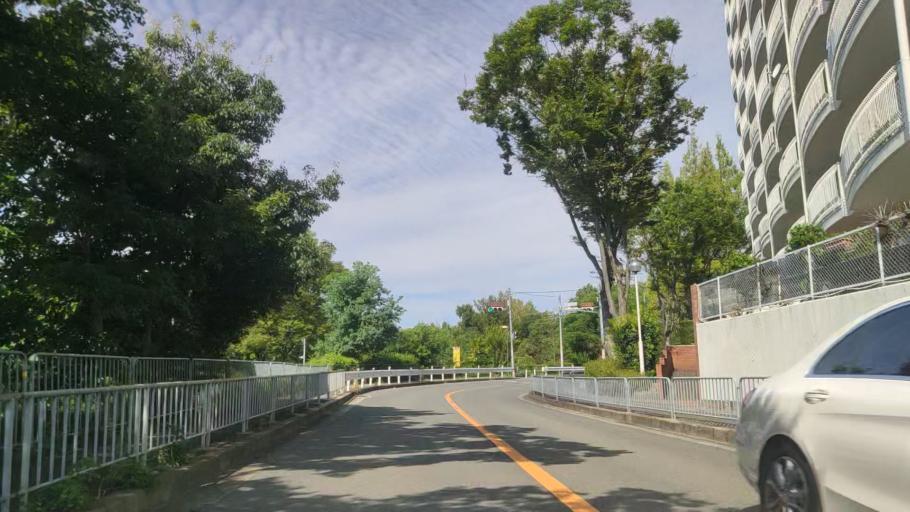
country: JP
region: Osaka
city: Mino
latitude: 34.8235
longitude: 135.5178
